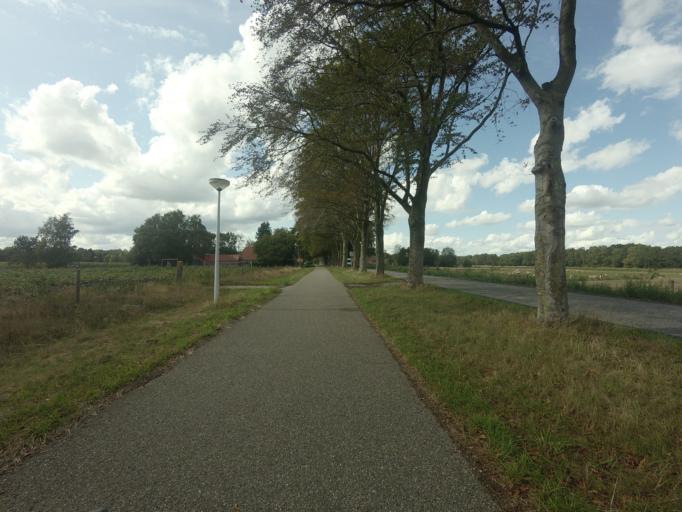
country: NL
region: Drenthe
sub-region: Gemeente Westerveld
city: Dwingeloo
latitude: 52.9542
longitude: 6.3343
